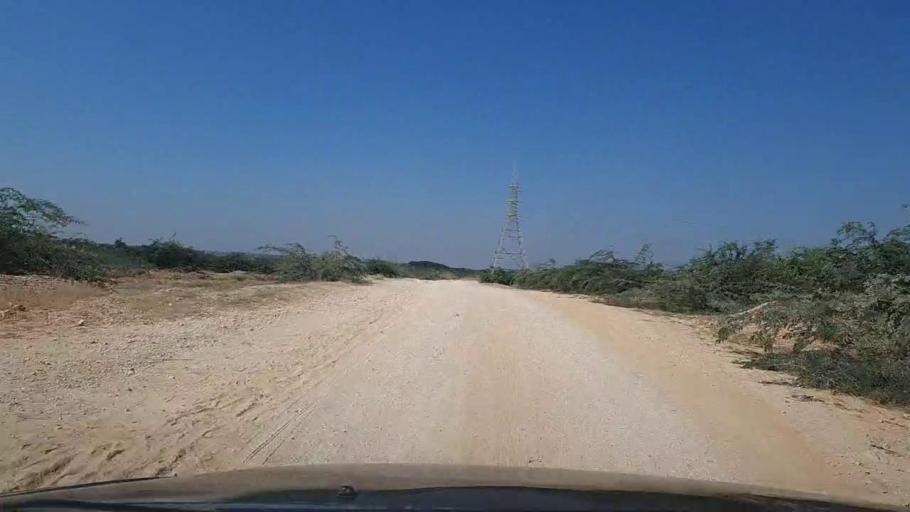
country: PK
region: Sindh
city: Thatta
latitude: 24.6240
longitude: 67.8372
